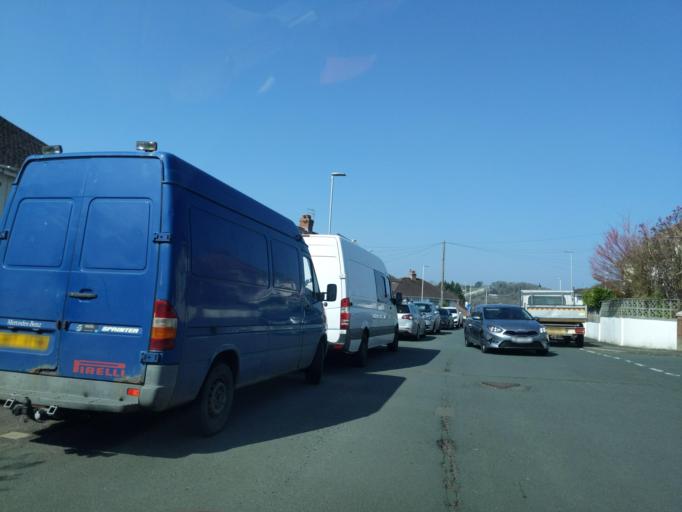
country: GB
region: England
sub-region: Devon
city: Plympton
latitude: 50.3920
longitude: -4.0774
